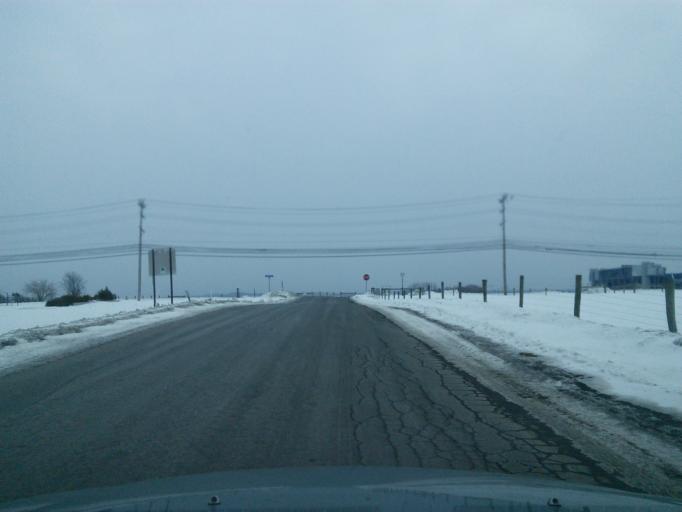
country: US
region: Pennsylvania
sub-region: Centre County
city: State College
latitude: 40.8209
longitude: -77.8570
